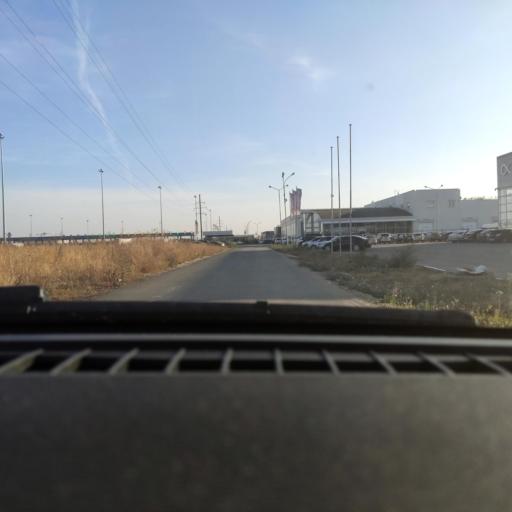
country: RU
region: Voronezj
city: Somovo
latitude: 51.6665
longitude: 39.2999
